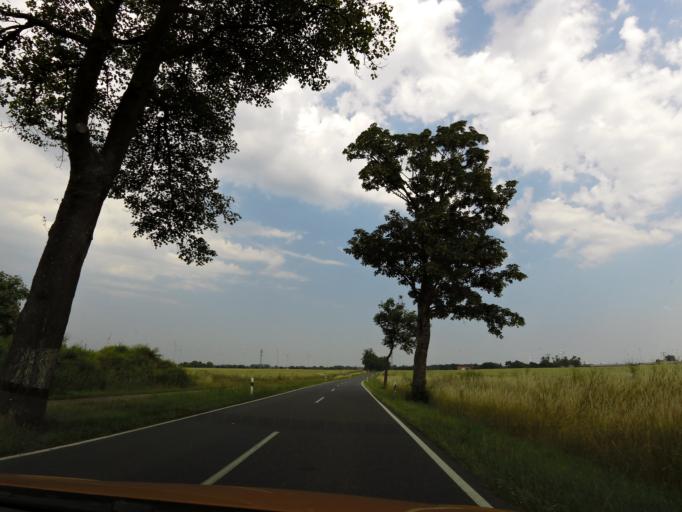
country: DE
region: Brandenburg
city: Nauen
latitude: 52.5637
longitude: 12.8694
